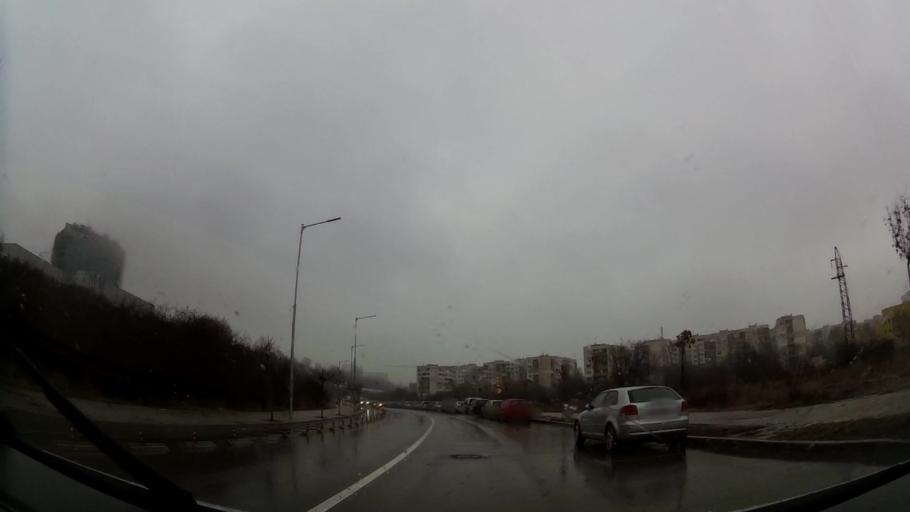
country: BG
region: Sofia-Capital
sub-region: Stolichna Obshtina
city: Sofia
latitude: 42.6503
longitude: 23.3986
